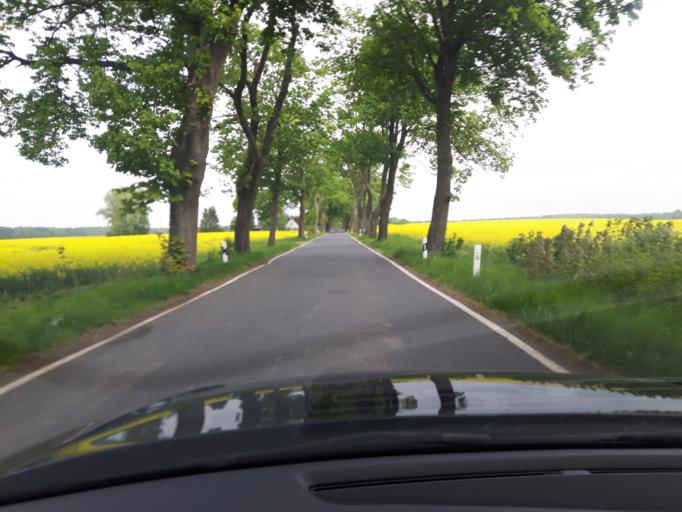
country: DE
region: Mecklenburg-Vorpommern
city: Velgast
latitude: 54.2094
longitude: 12.7324
